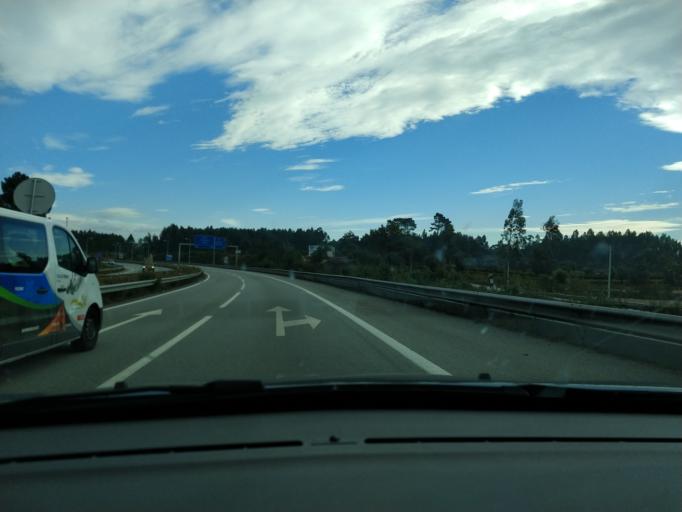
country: PT
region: Aveiro
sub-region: Albergaria-A-Velha
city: Albergaria-a-Velha
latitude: 40.6822
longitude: -8.5301
